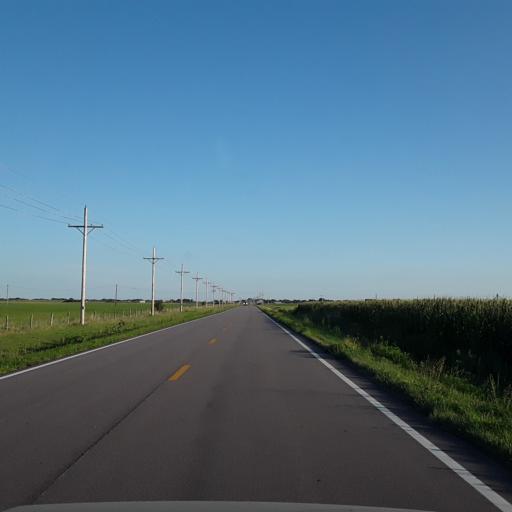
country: US
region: Nebraska
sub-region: Hall County
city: Grand Island
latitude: 40.9656
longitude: -98.3207
